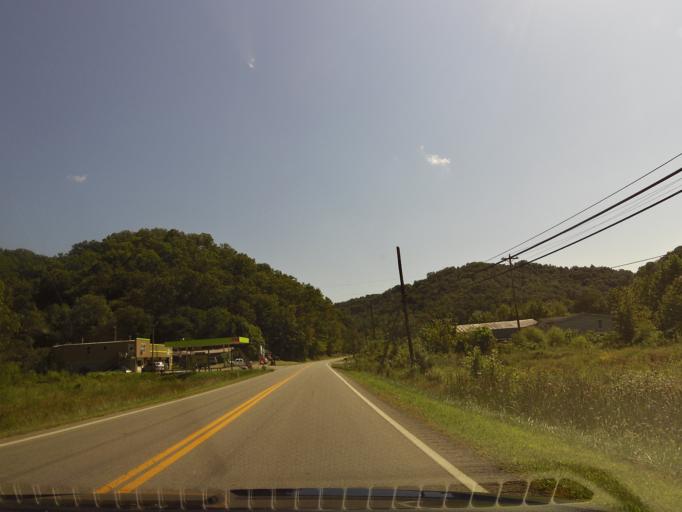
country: US
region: Kentucky
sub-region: Clay County
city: Manchester
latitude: 37.1161
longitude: -83.7257
